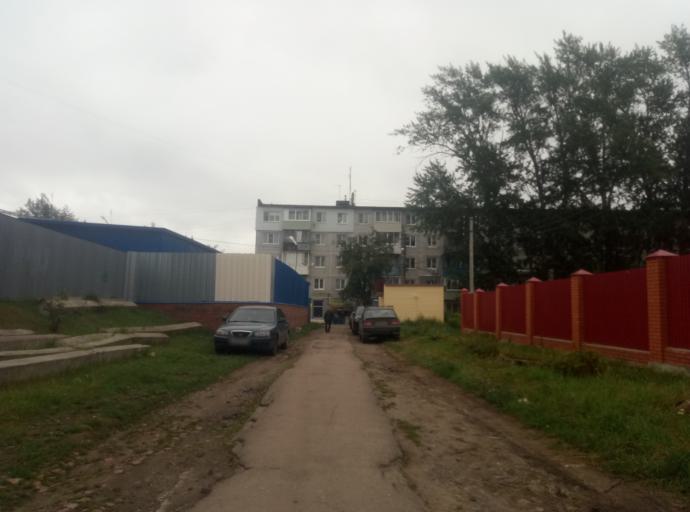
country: RU
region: Tula
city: Kireyevsk
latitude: 53.9253
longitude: 37.9299
